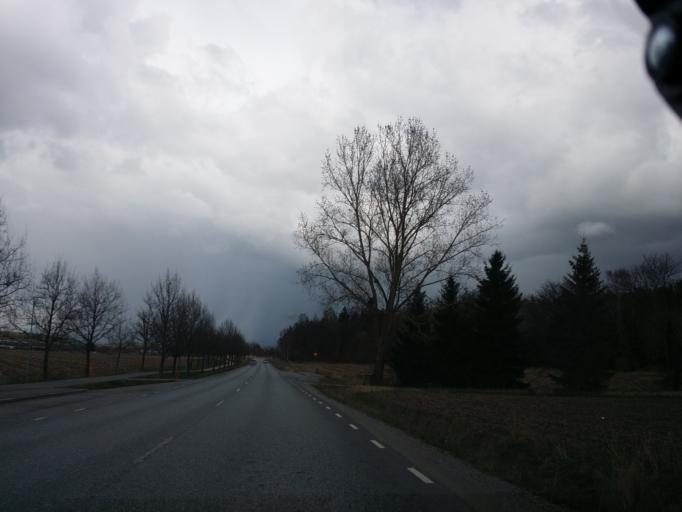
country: SE
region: Uppsala
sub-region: Enkopings Kommun
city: Enkoping
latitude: 59.6185
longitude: 17.0791
